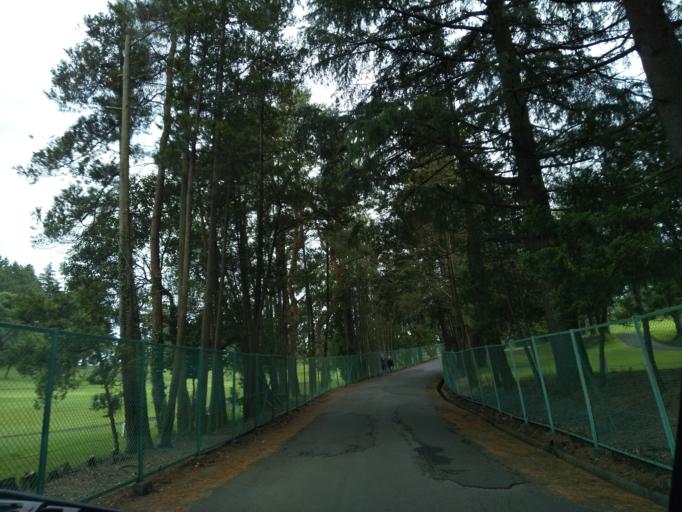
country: JP
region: Kanagawa
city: Atsugi
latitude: 35.4764
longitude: 139.3240
